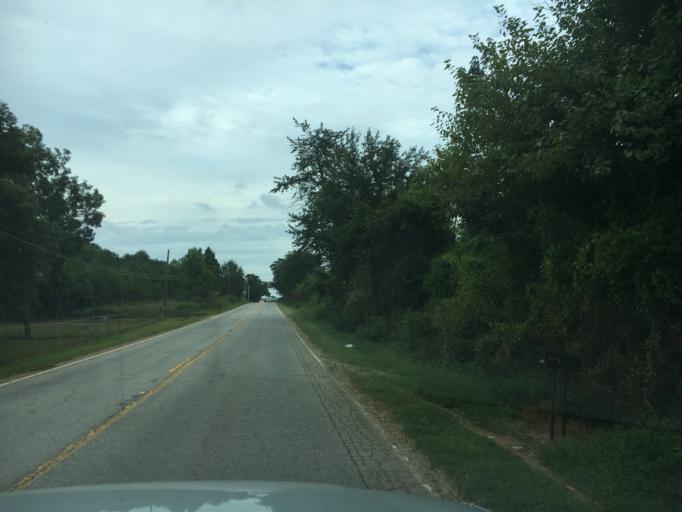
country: US
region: South Carolina
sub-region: Greenville County
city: Greer
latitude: 34.9349
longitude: -82.2003
